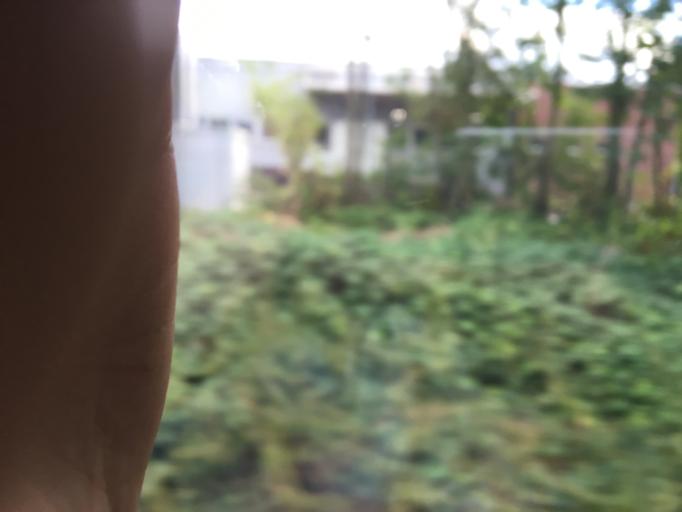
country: DE
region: North Rhine-Westphalia
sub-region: Regierungsbezirk Arnsberg
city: Dortmund
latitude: 51.5091
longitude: 7.3960
